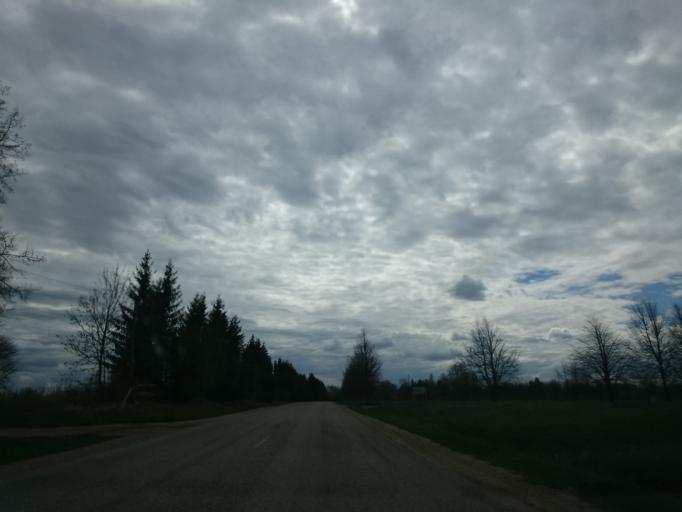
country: LV
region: Aizpute
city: Aizpute
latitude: 56.7414
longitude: 21.6094
